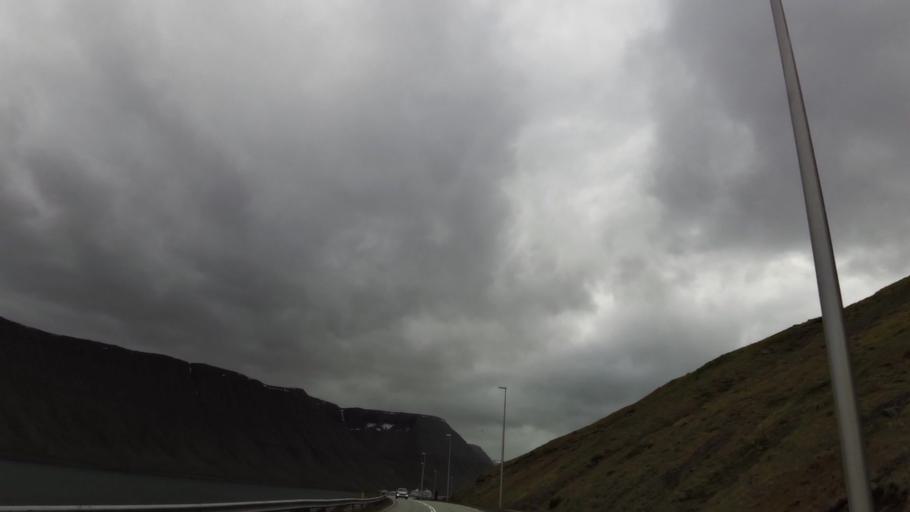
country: IS
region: Westfjords
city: Isafjoerdur
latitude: 66.0939
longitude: -23.1132
